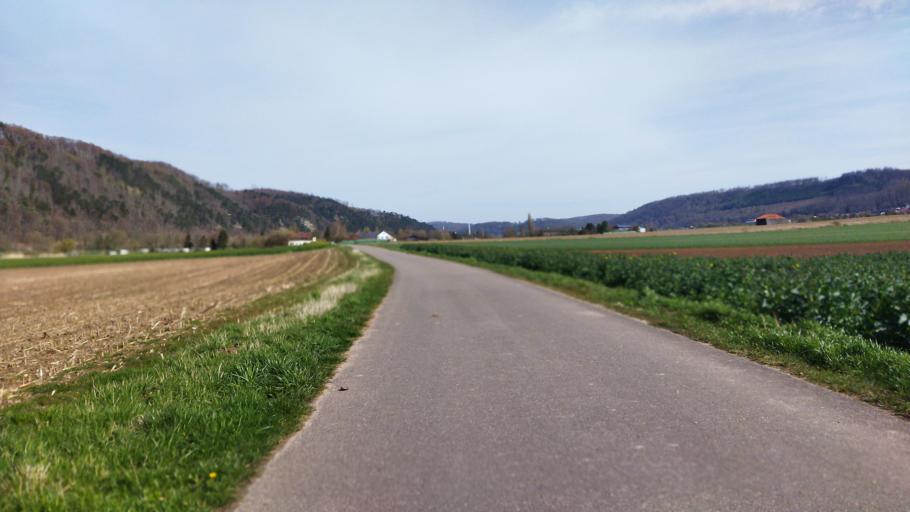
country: DE
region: Lower Saxony
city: Bodenwerder
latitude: 51.9535
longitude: 9.5050
